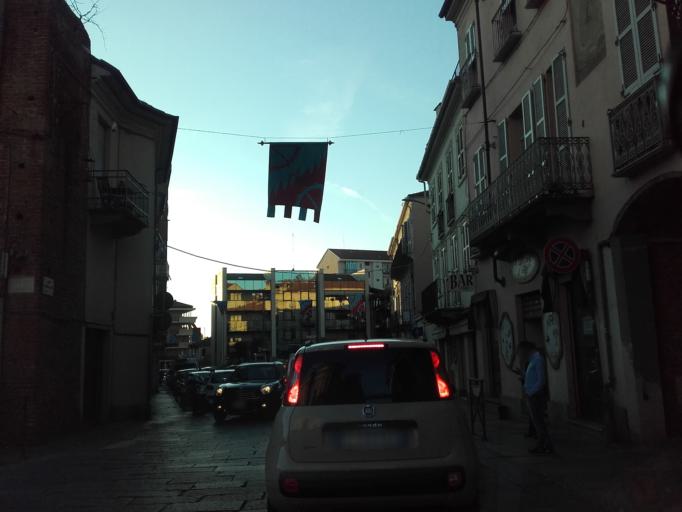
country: IT
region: Piedmont
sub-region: Provincia di Asti
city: Asti
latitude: 44.8988
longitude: 8.1953
